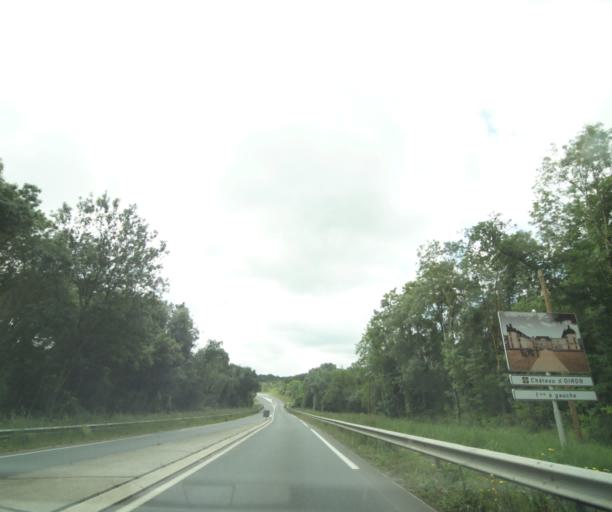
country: FR
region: Poitou-Charentes
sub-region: Departement des Deux-Sevres
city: Saint-Varent
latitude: 46.9161
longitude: -0.1962
